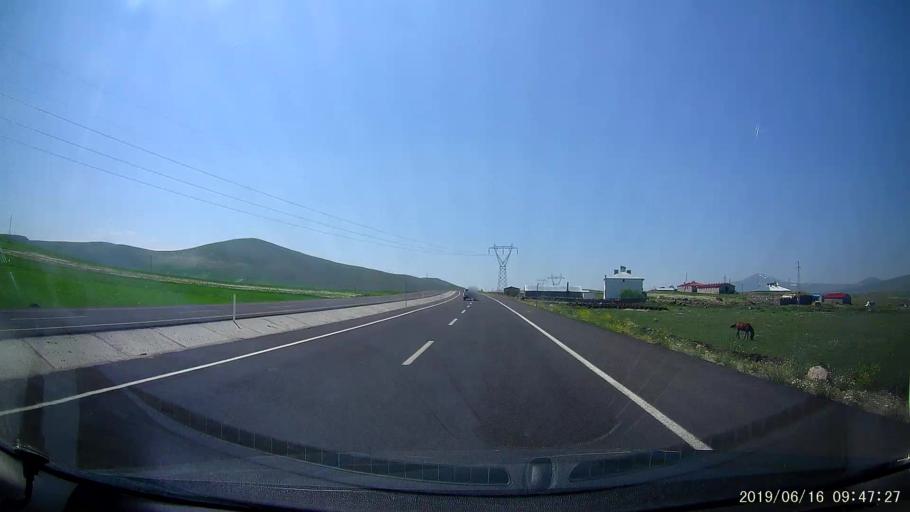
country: TR
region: Kars
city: Digor
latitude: 40.4475
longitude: 43.3438
